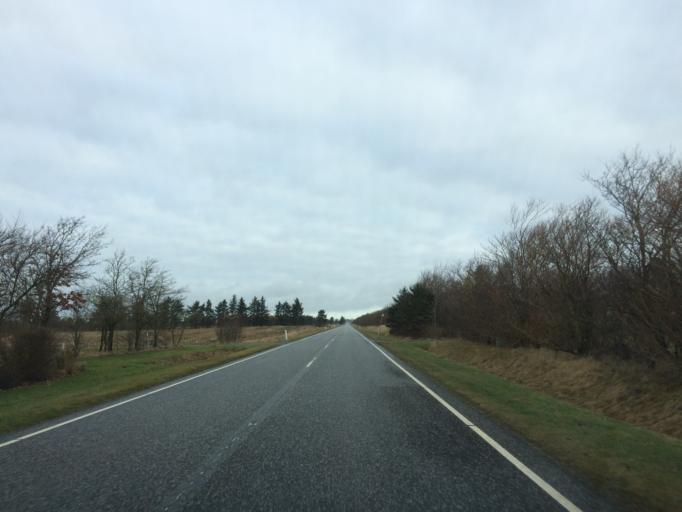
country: DK
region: Central Jutland
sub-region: Holstebro Kommune
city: Holstebro
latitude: 56.3837
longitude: 8.4513
